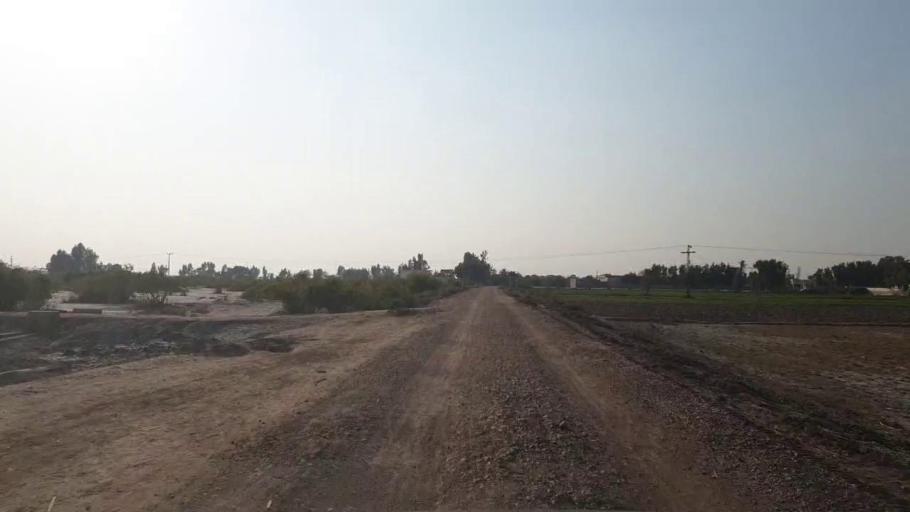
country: PK
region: Sindh
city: Mirpur Khas
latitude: 25.4390
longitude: 68.9424
